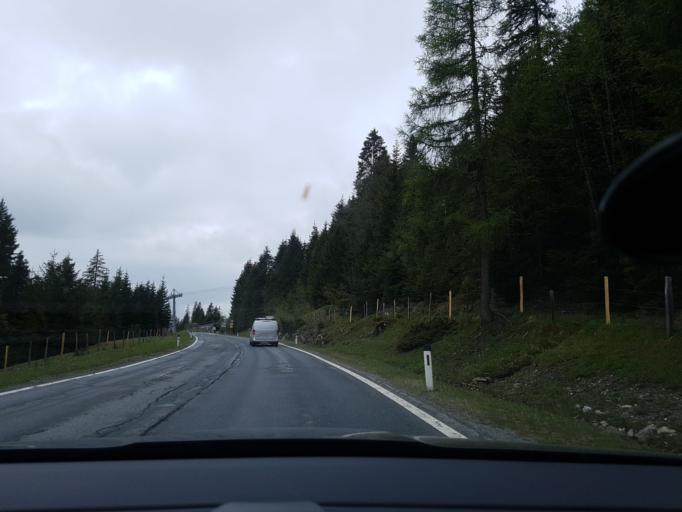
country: AT
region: Salzburg
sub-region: Politischer Bezirk Zell am See
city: Krimml
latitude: 47.2438
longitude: 12.1165
